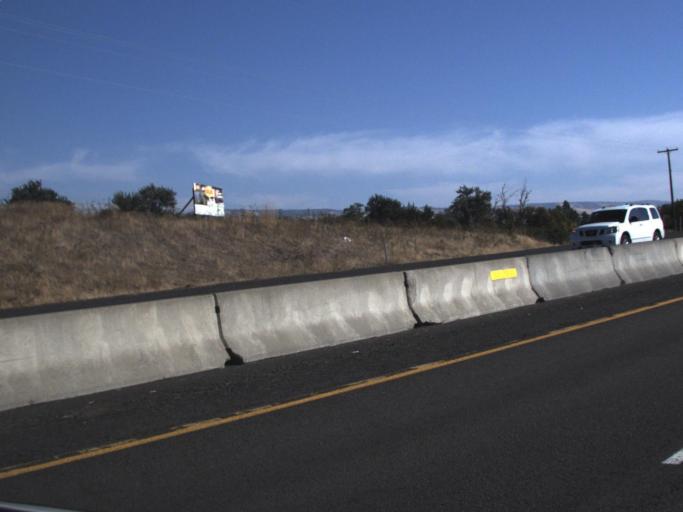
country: US
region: Washington
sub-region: Walla Walla County
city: College Place
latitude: 46.0045
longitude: -118.3887
